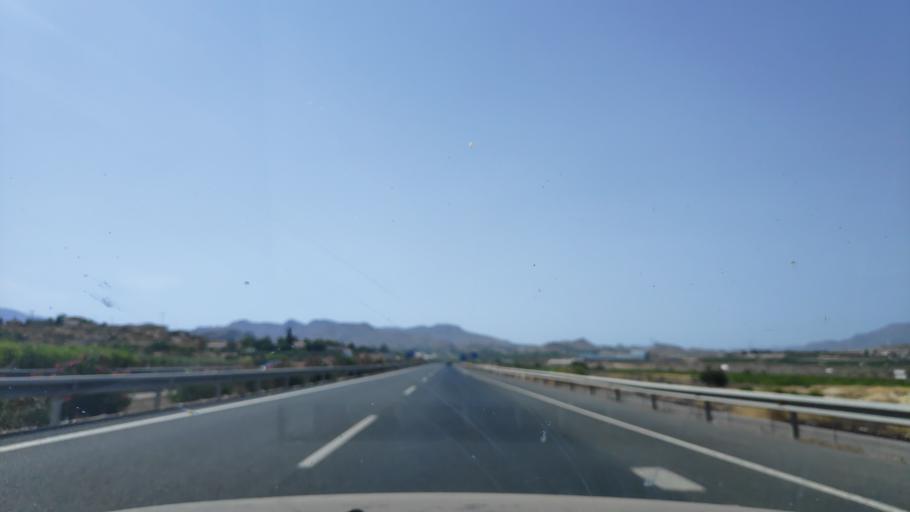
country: ES
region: Murcia
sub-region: Murcia
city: Archena
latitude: 38.1278
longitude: -1.2594
